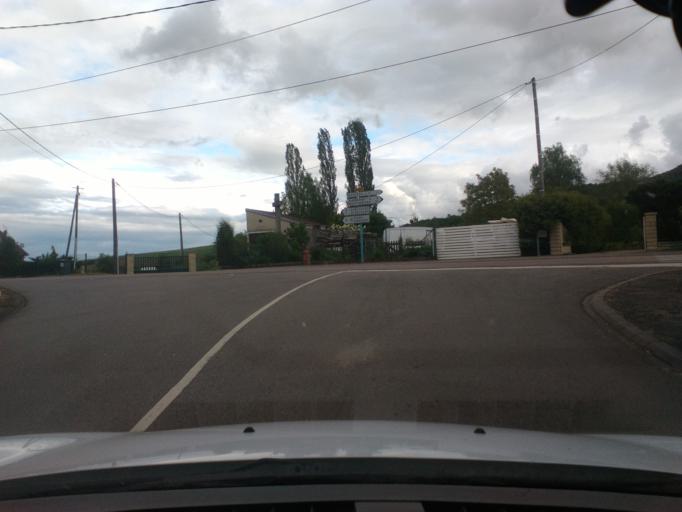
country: FR
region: Lorraine
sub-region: Departement des Vosges
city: Mirecourt
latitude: 48.3099
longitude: 6.0543
